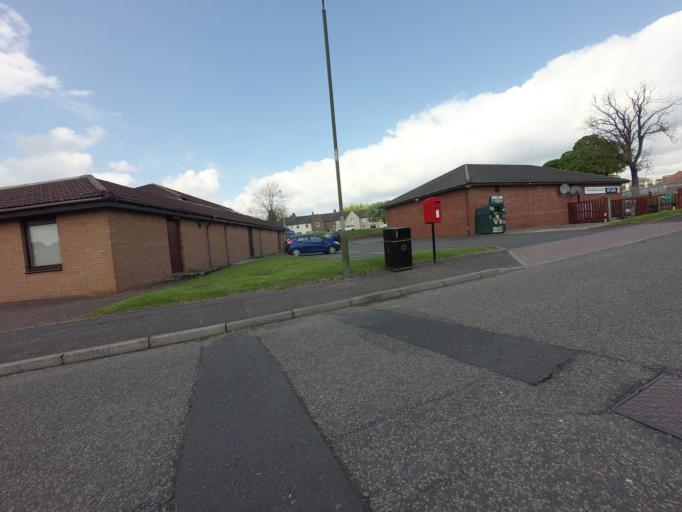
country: GB
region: Scotland
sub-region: Falkirk
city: Falkirk
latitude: 56.0241
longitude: -3.7928
